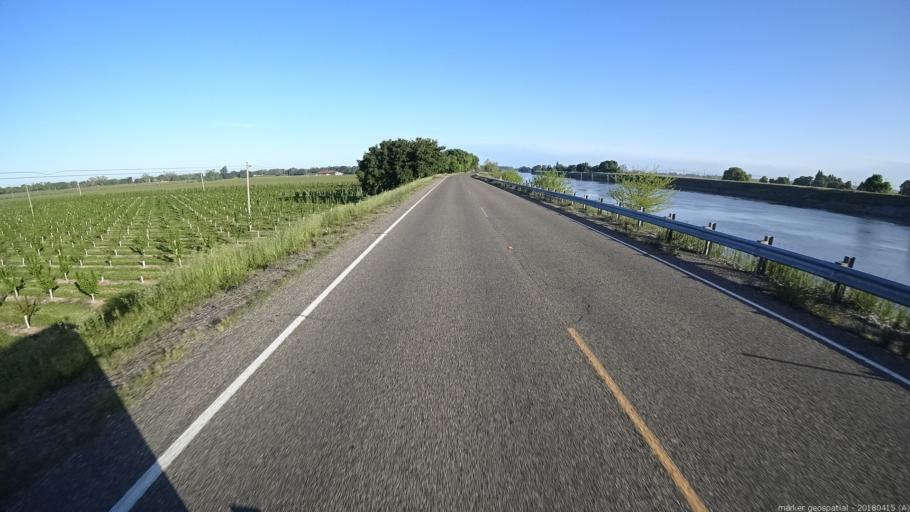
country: US
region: California
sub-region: Sacramento County
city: Walnut Grove
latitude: 38.2972
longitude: -121.5680
